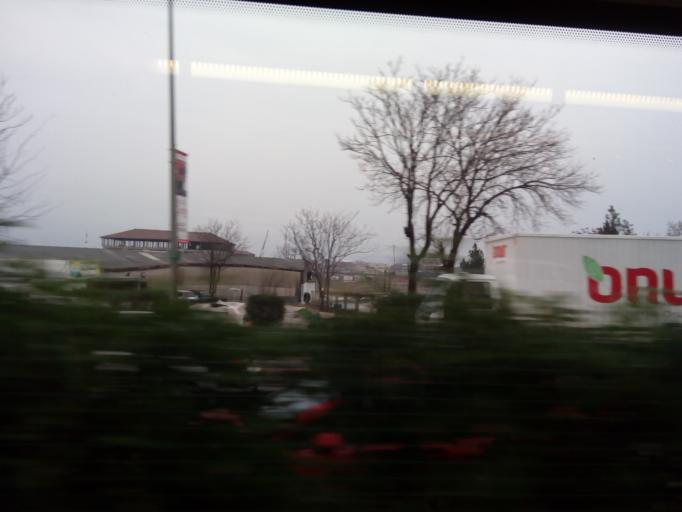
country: TR
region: Bursa
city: Yildirim
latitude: 40.2009
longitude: 29.0389
